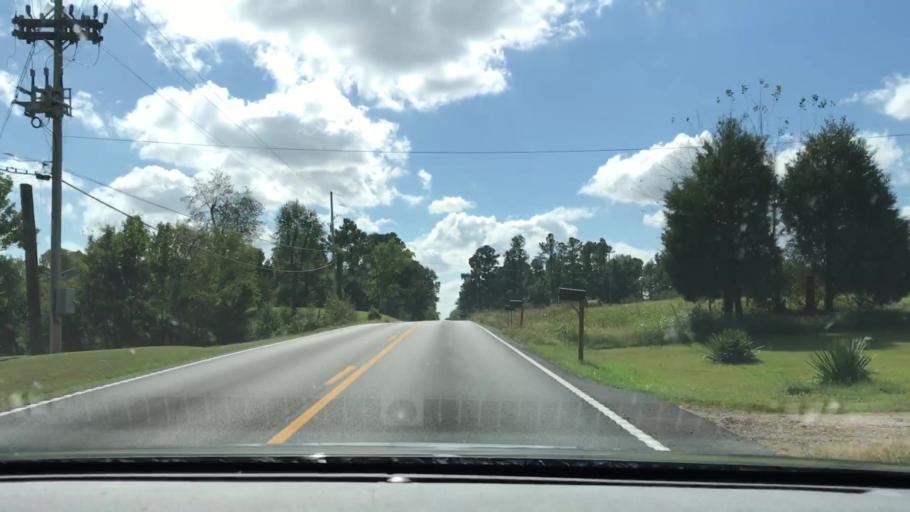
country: US
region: Kentucky
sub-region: Graves County
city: Mayfield
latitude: 36.7832
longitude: -88.5958
